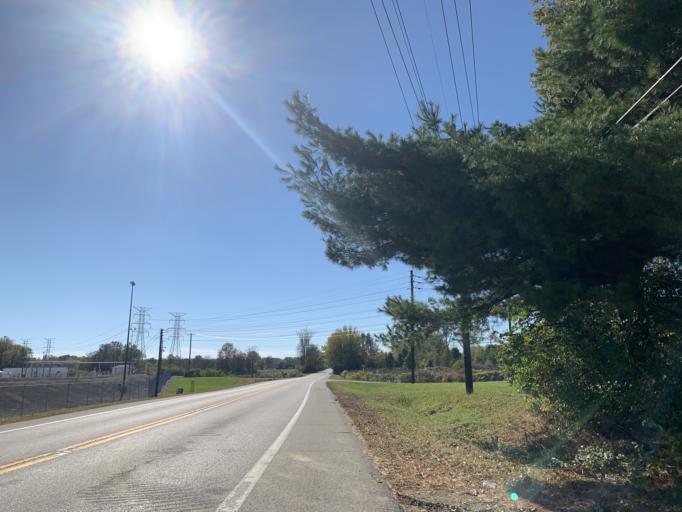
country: US
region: Kentucky
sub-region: Jefferson County
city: Saint Dennis
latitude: 38.2064
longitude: -85.8493
